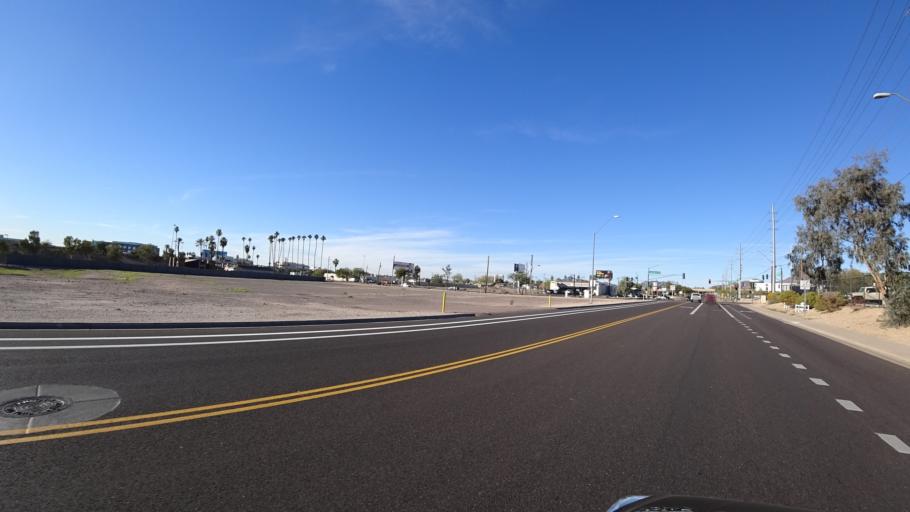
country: US
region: Arizona
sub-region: Maricopa County
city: Tempe Junction
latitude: 33.4500
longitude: -111.9784
